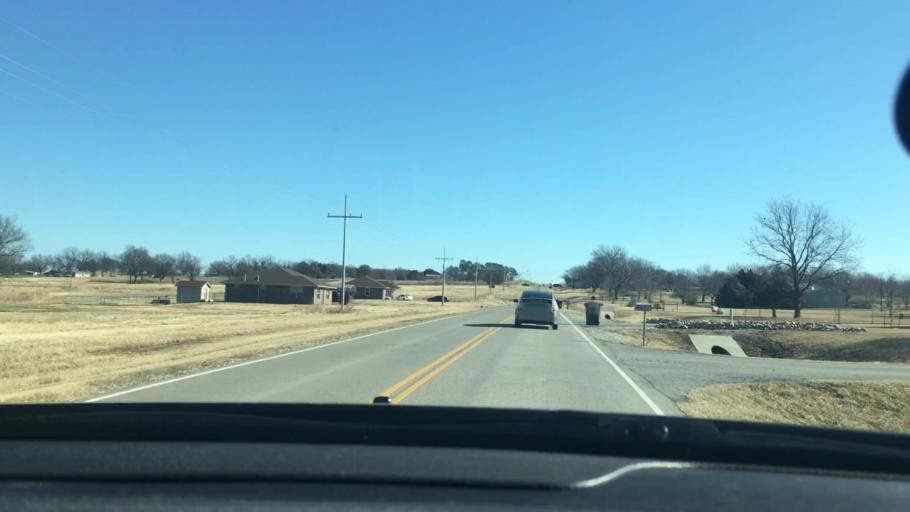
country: US
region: Oklahoma
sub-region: Murray County
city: Davis
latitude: 34.4772
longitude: -97.0631
